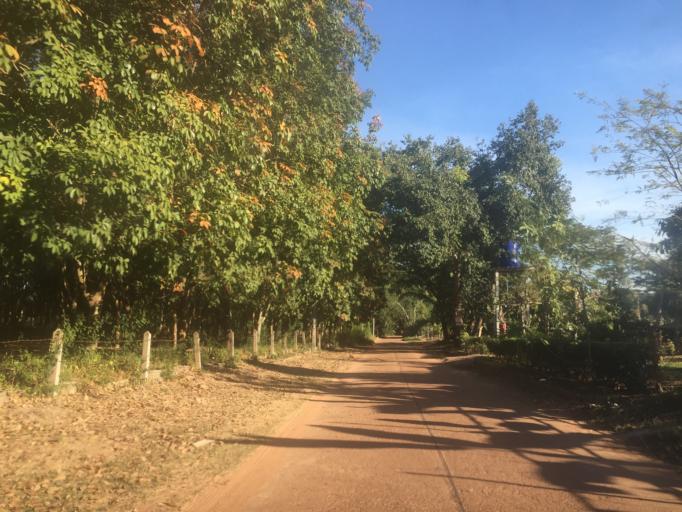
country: TH
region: Changwat Udon Thani
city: Si That
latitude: 16.9704
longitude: 103.2279
